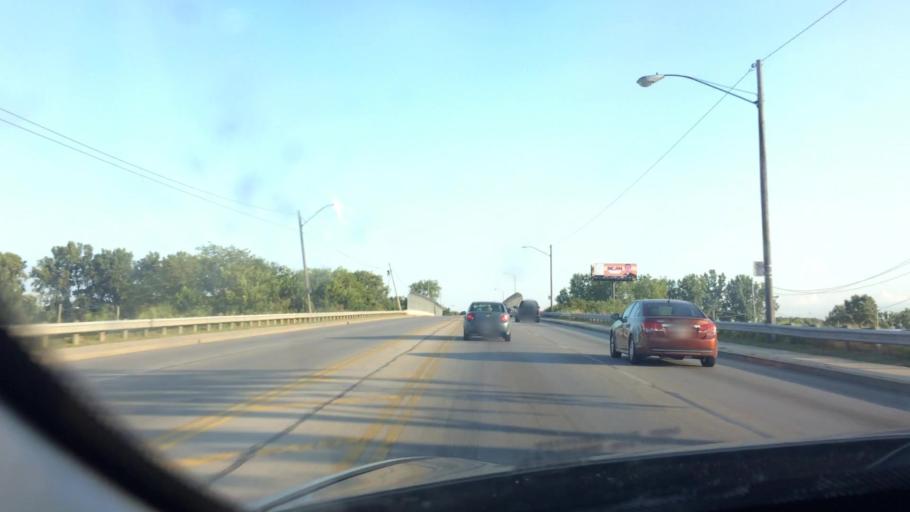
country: US
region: Ohio
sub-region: Lucas County
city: Ottawa Hills
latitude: 41.6333
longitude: -83.6259
